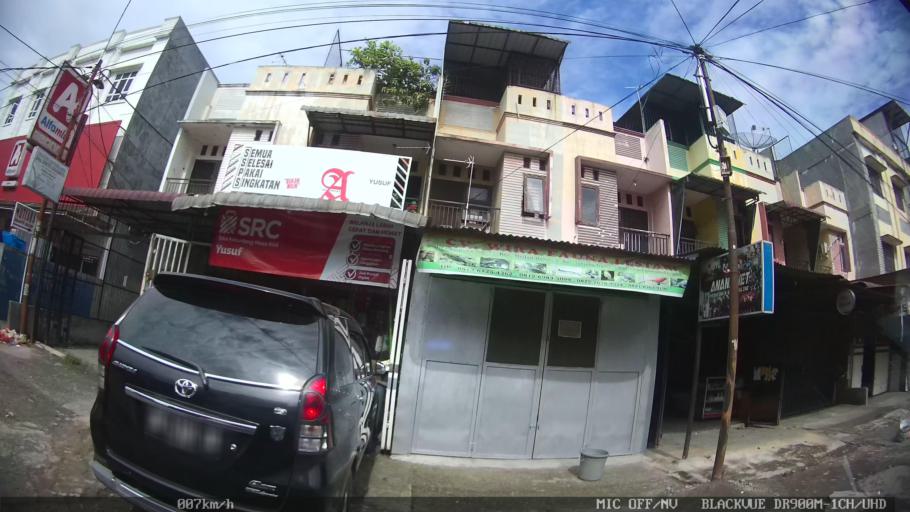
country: ID
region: North Sumatra
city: Sunggal
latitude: 3.6075
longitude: 98.6120
